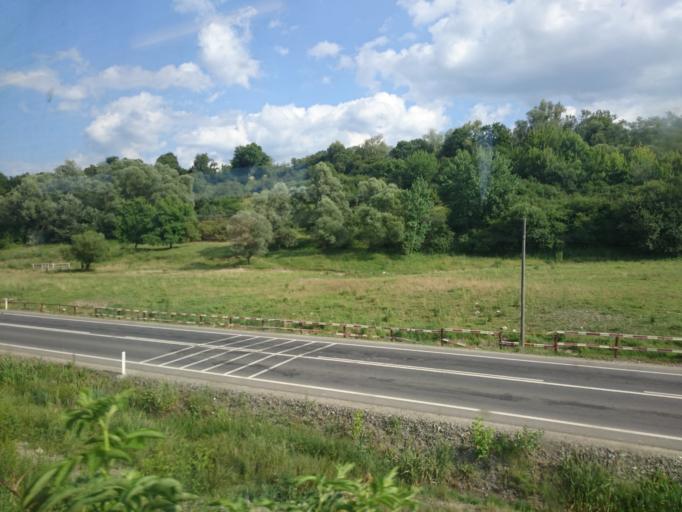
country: RO
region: Sibiu
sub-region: Oras Dumbraveni
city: Dumbraveni
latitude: 46.2166
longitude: 24.5726
